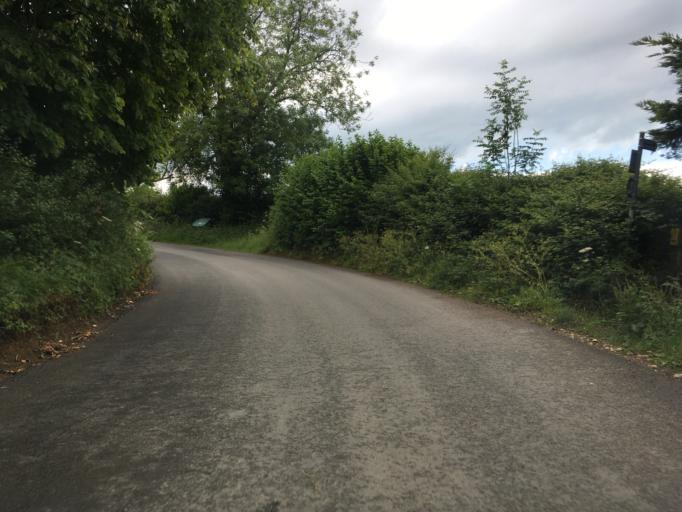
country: GB
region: England
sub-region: Gloucestershire
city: Shurdington
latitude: 51.8260
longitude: -2.1067
